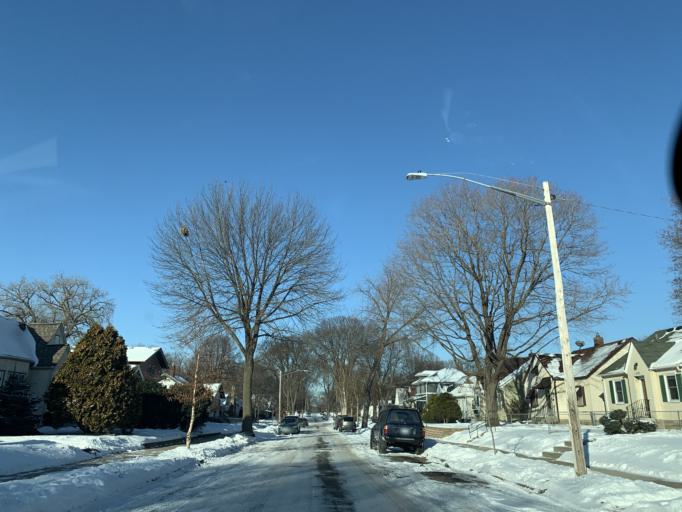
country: US
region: Minnesota
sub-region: Dakota County
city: Mendota Heights
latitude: 44.9059
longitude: -93.2089
